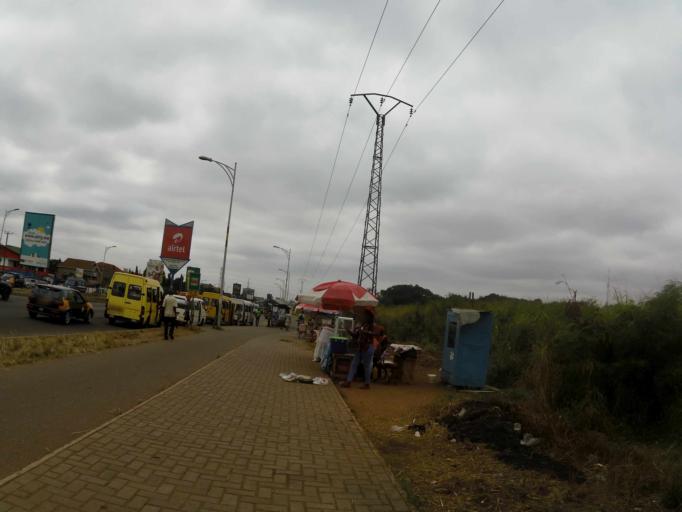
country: GH
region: Greater Accra
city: Medina Estates
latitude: 5.6403
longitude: -0.1783
